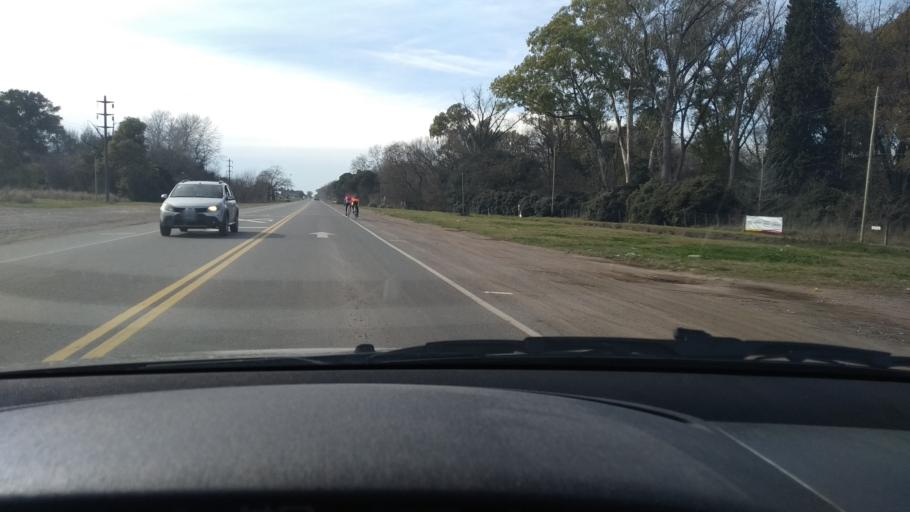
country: AR
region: Buenos Aires
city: Olavarria
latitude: -36.9602
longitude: -60.2597
